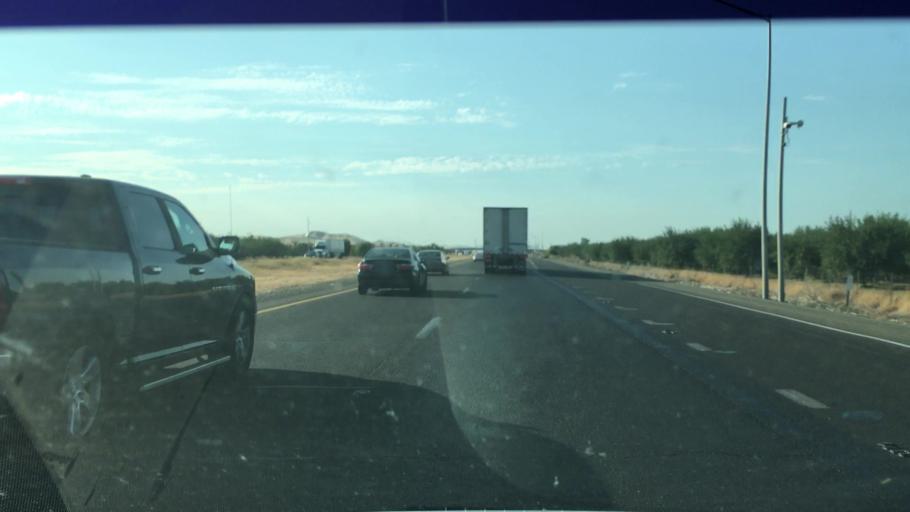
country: US
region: California
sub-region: Merced County
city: Gustine
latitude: 37.1234
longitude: -121.0269
